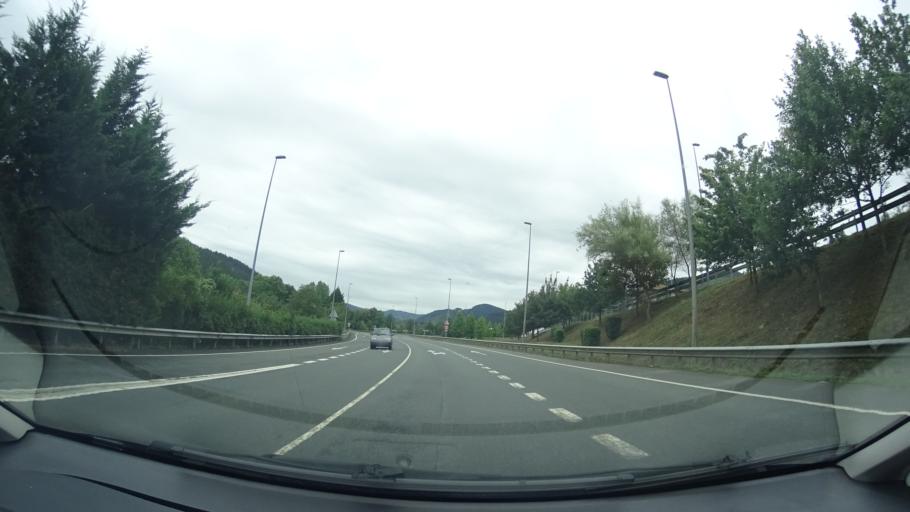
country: ES
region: Basque Country
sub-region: Bizkaia
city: Areatza
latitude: 43.1375
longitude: -2.7848
